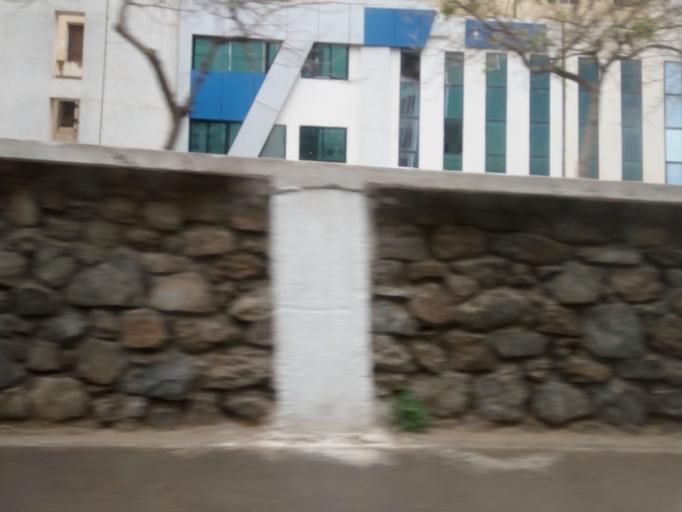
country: DZ
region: Tipaza
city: Saoula
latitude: 36.7336
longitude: 2.9934
